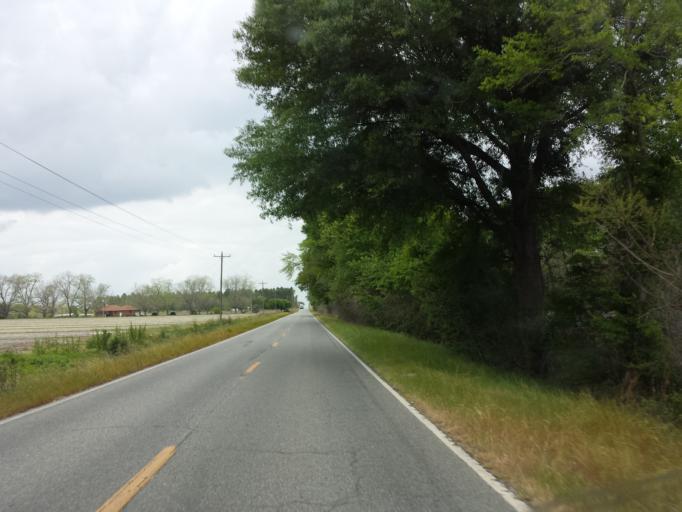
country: US
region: Georgia
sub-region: Cook County
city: Sparks
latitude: 31.2863
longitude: -83.4680
